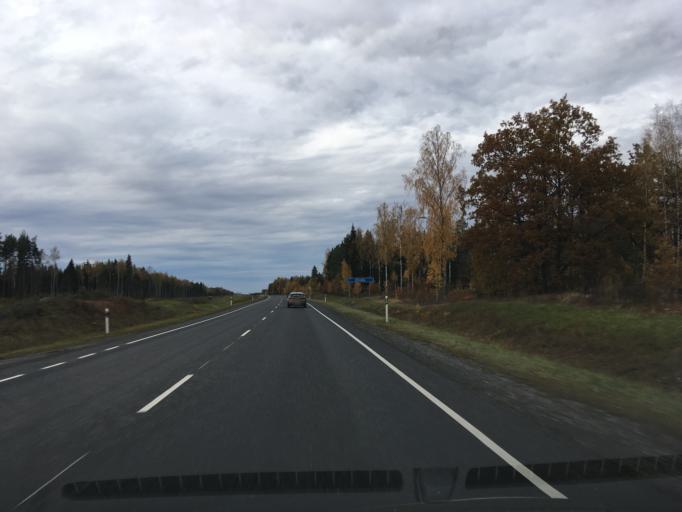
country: EE
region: Harju
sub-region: Nissi vald
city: Turba
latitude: 58.9503
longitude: 24.0825
